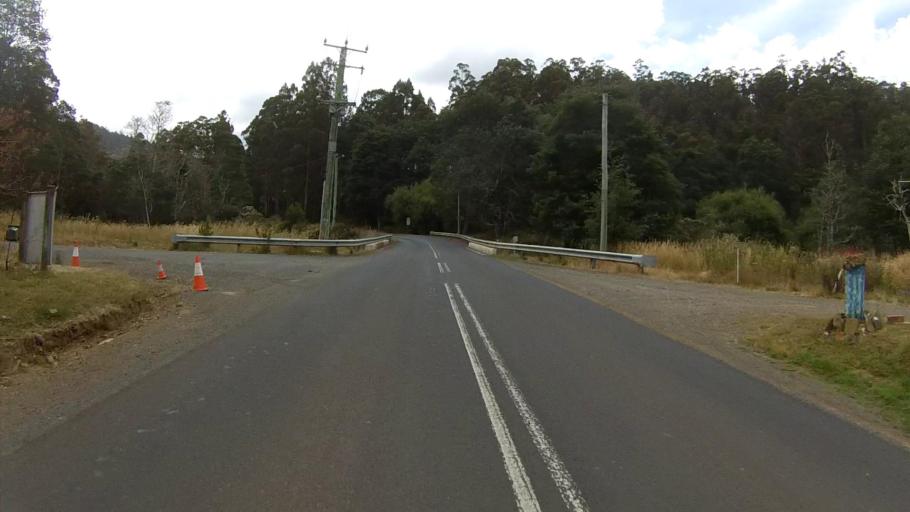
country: AU
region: Tasmania
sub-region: Huon Valley
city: Cygnet
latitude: -43.1420
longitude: 147.1536
